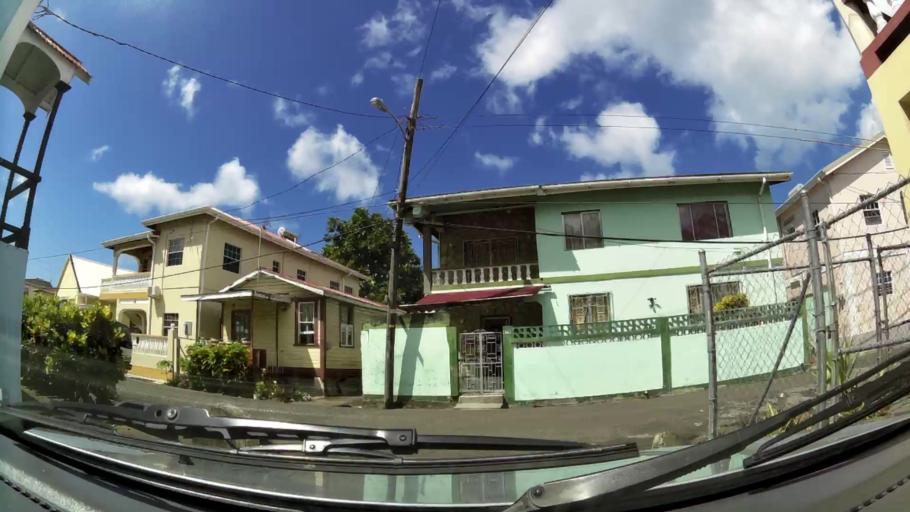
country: GD
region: Saint John
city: Gouyave
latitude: 12.1672
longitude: -61.7288
